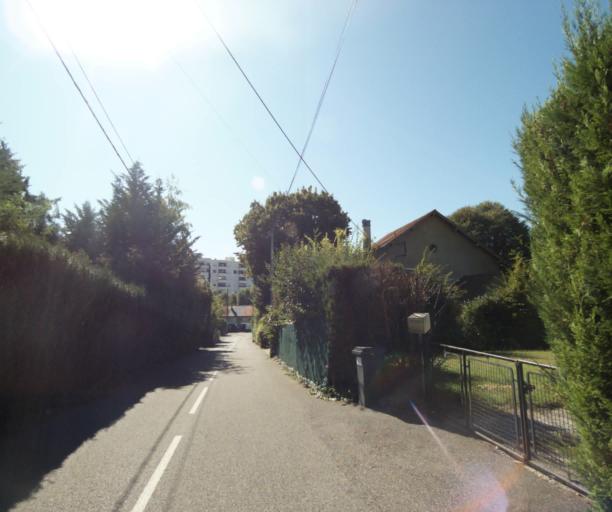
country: FR
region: Rhone-Alpes
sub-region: Departement de l'Ain
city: Ferney-Voltaire
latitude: 46.2543
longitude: 6.1151
